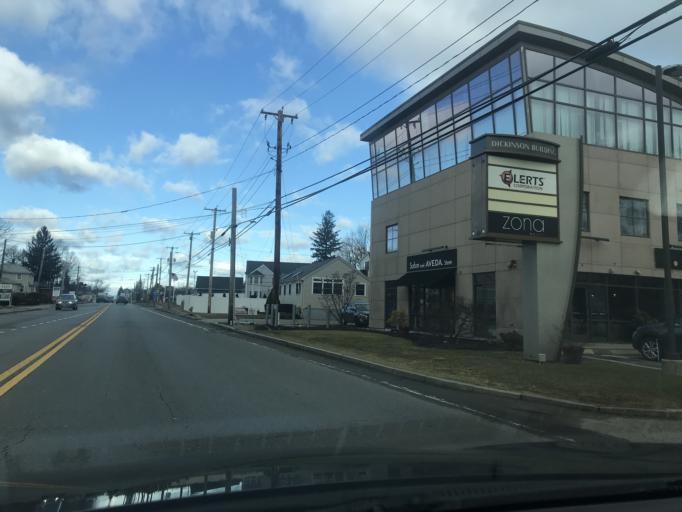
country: US
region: Massachusetts
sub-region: Plymouth County
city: Rockland
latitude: 42.1652
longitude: -70.9552
